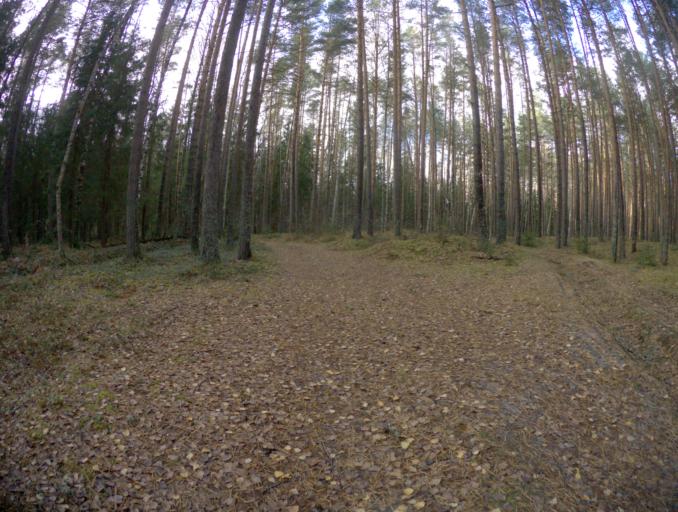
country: RU
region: Vladimir
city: Raduzhnyy
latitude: 56.0569
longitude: 40.3243
